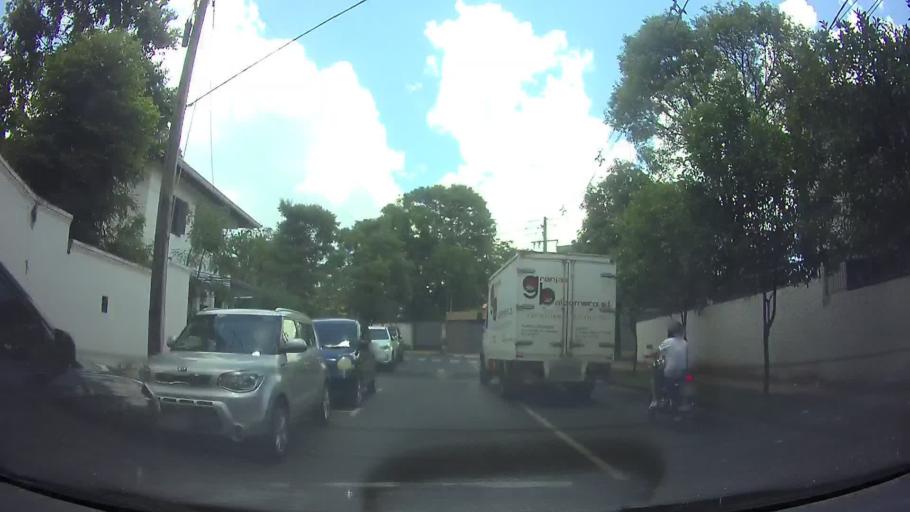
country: PY
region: Asuncion
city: Asuncion
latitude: -25.2954
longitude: -57.5989
